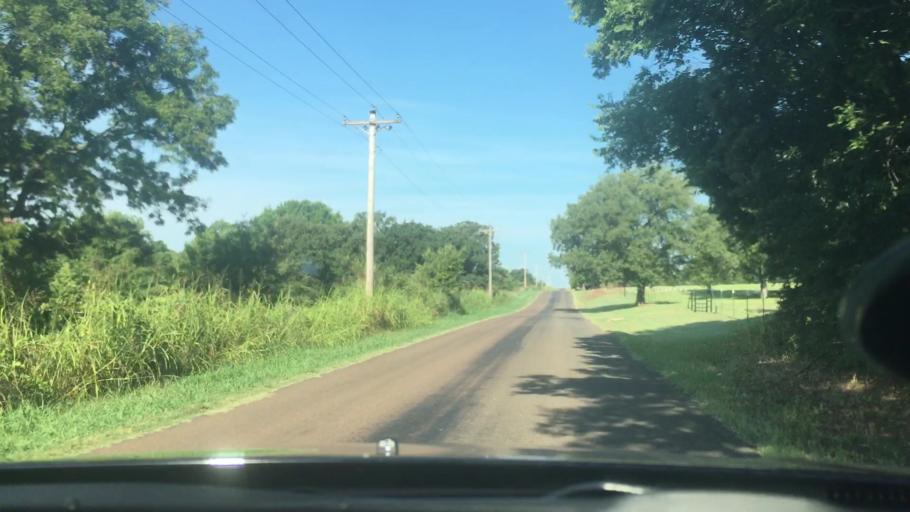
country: US
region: Oklahoma
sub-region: Garvin County
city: Pauls Valley
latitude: 34.6521
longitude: -97.3651
